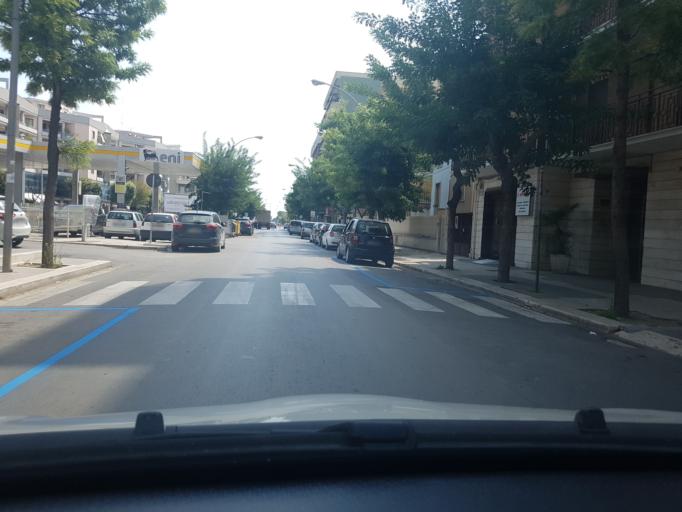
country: IT
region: Apulia
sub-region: Provincia di Foggia
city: Cerignola
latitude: 41.2633
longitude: 15.9107
